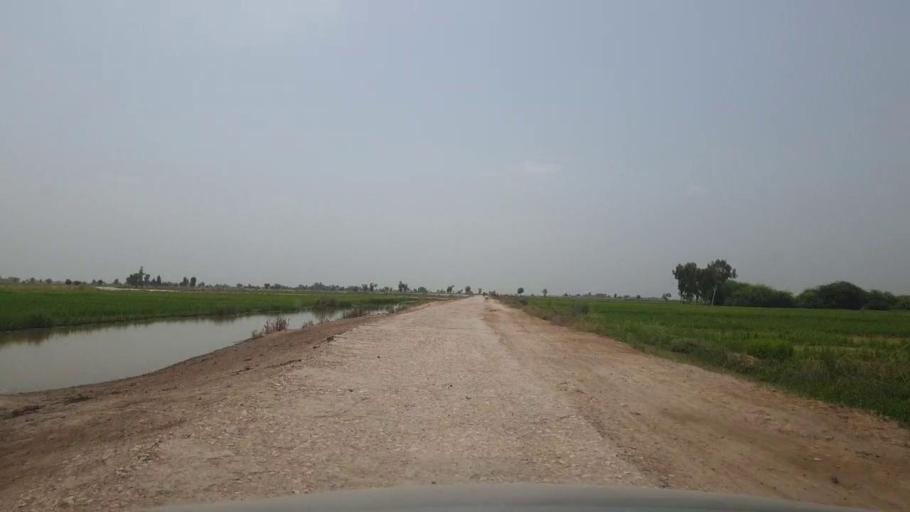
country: PK
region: Sindh
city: Garhi Yasin
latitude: 27.9397
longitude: 68.3894
